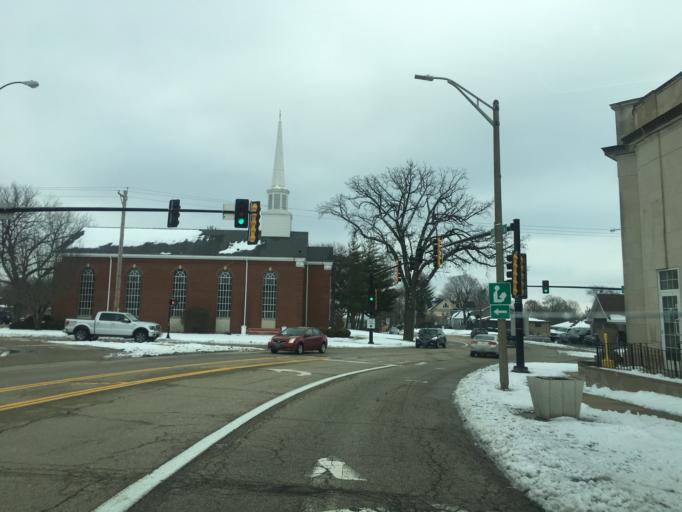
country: US
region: Illinois
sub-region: LaSalle County
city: Peru
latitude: 41.3276
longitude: -89.1257
